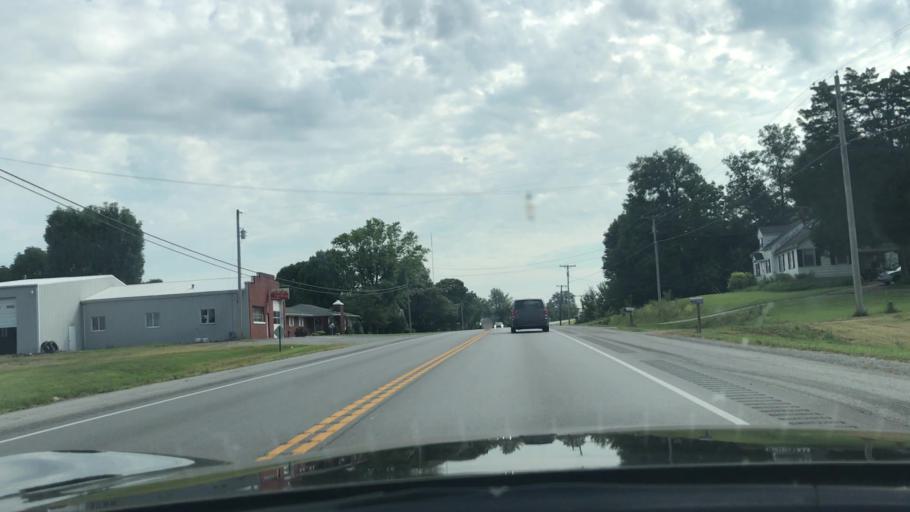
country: US
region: Kentucky
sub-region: Taylor County
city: Campbellsville
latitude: 37.3300
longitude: -85.3849
